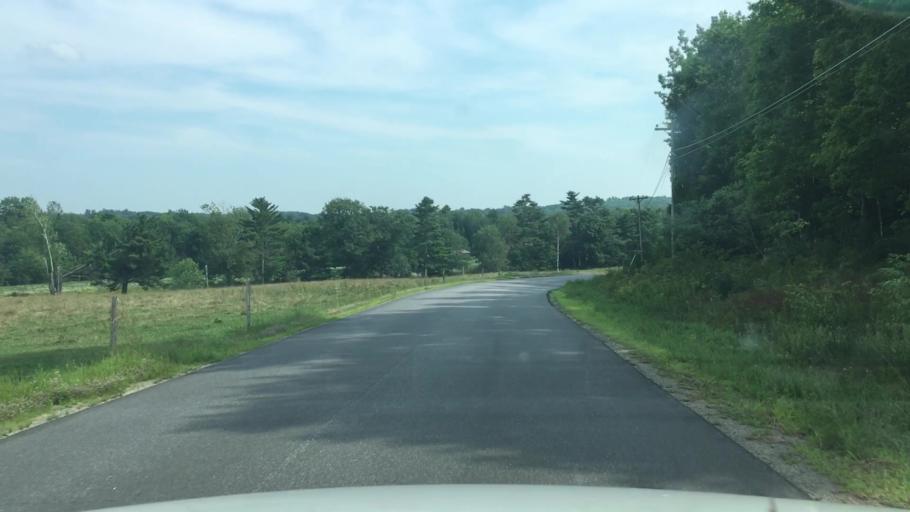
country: US
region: Maine
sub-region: Lincoln County
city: Jefferson
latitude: 44.2163
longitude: -69.4479
